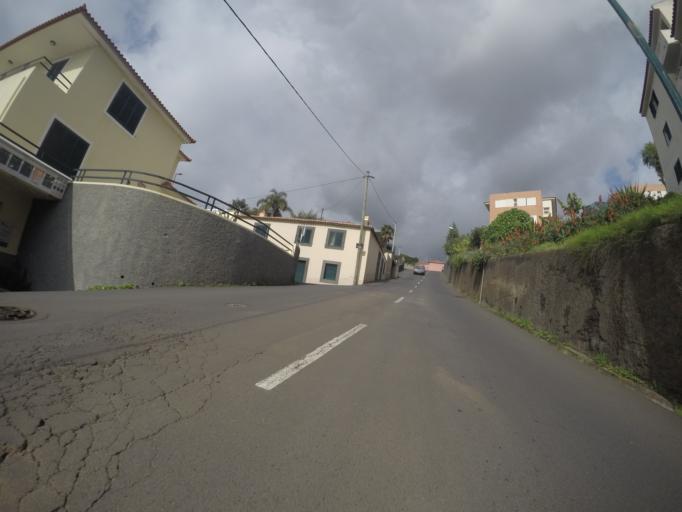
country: PT
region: Madeira
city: Camara de Lobos
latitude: 32.6600
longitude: -16.9443
